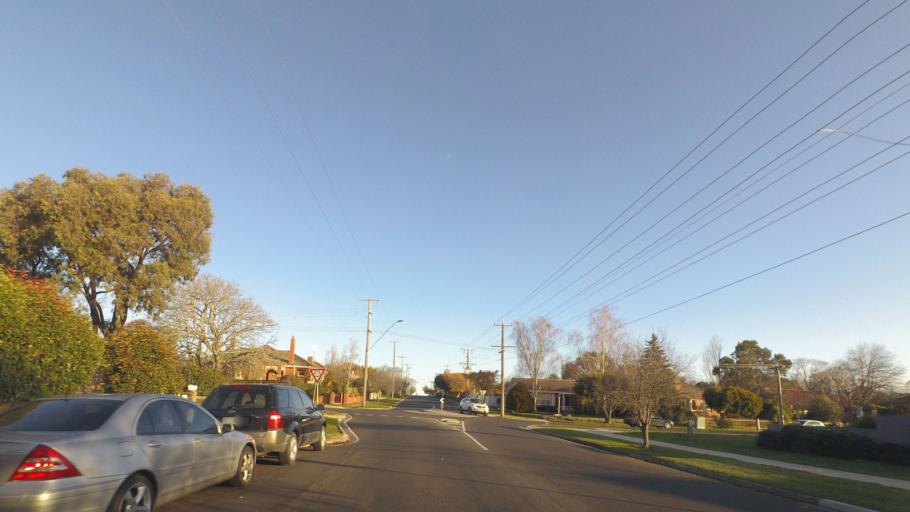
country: AU
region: Victoria
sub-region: Mount Alexander
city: Castlemaine
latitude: -37.2516
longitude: 144.4623
